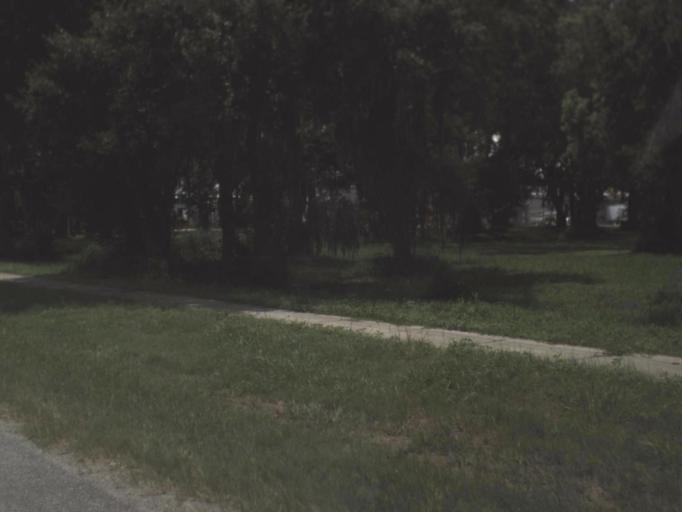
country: US
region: Florida
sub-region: Hillsborough County
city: Dover
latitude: 27.9911
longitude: -82.2349
